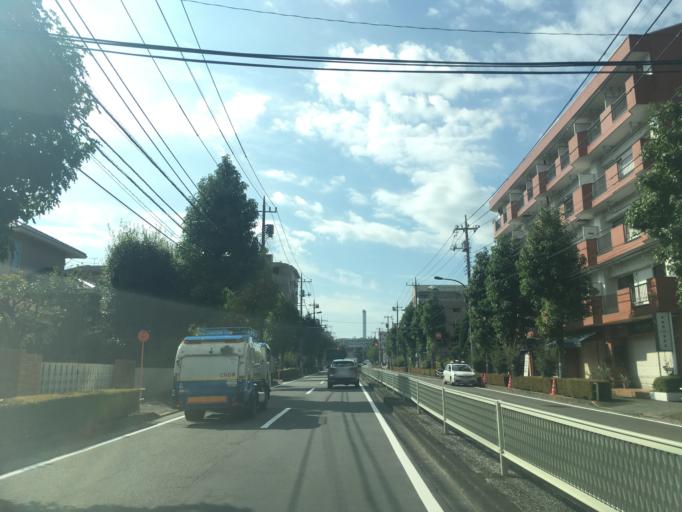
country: JP
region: Tokyo
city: Hino
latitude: 35.6210
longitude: 139.4158
